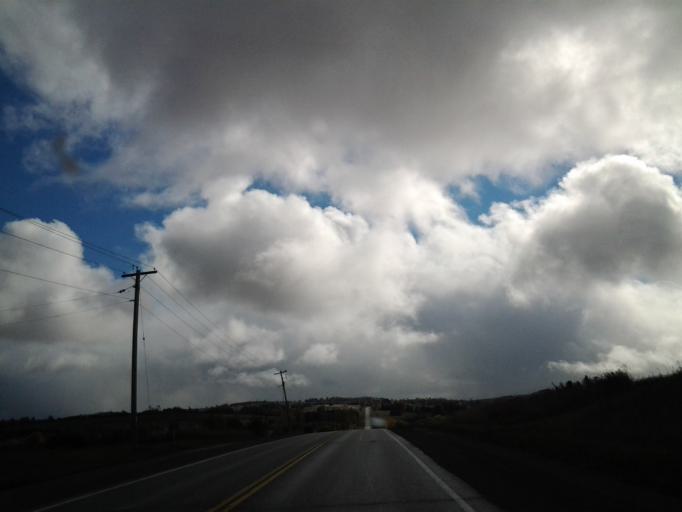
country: CA
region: Ontario
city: Shelburne
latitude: 44.1339
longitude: -80.0296
